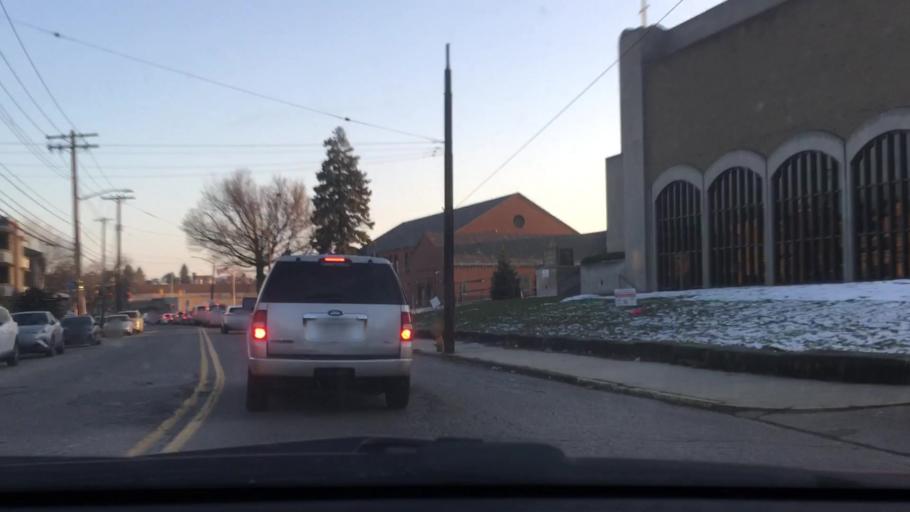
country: US
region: Pennsylvania
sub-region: Allegheny County
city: Brentwood
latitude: 40.3885
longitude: -79.9850
